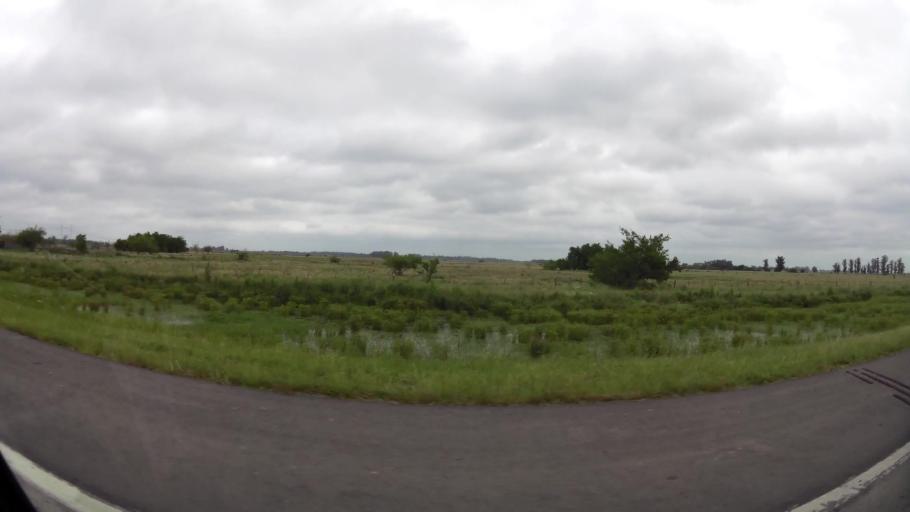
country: AR
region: Buenos Aires
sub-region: Partido de Brandsen
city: Brandsen
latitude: -35.0470
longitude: -58.1432
